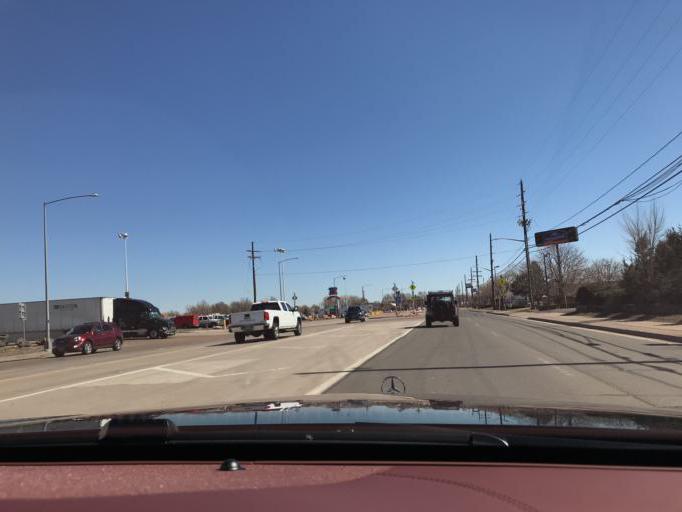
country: US
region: Colorado
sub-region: Jefferson County
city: Applewood
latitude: 39.7783
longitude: -105.1363
